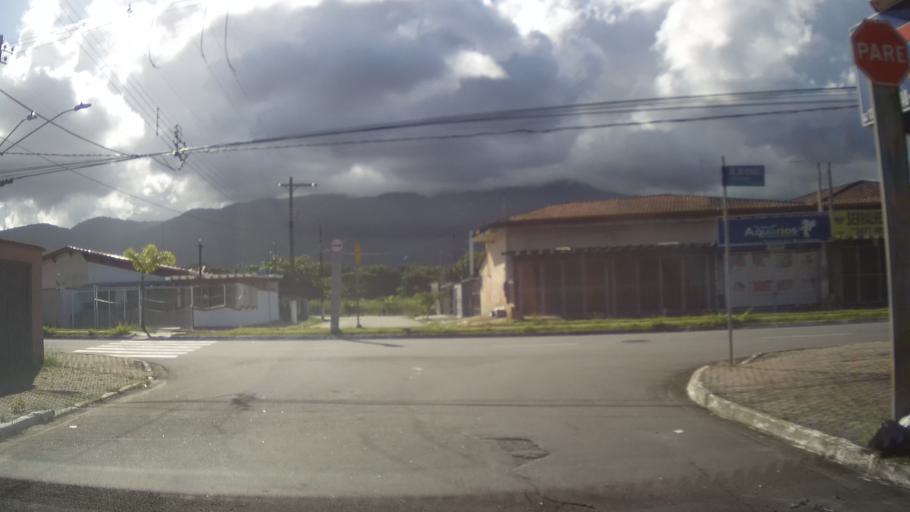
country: BR
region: Sao Paulo
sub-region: Mongagua
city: Mongagua
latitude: -24.0563
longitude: -46.5492
